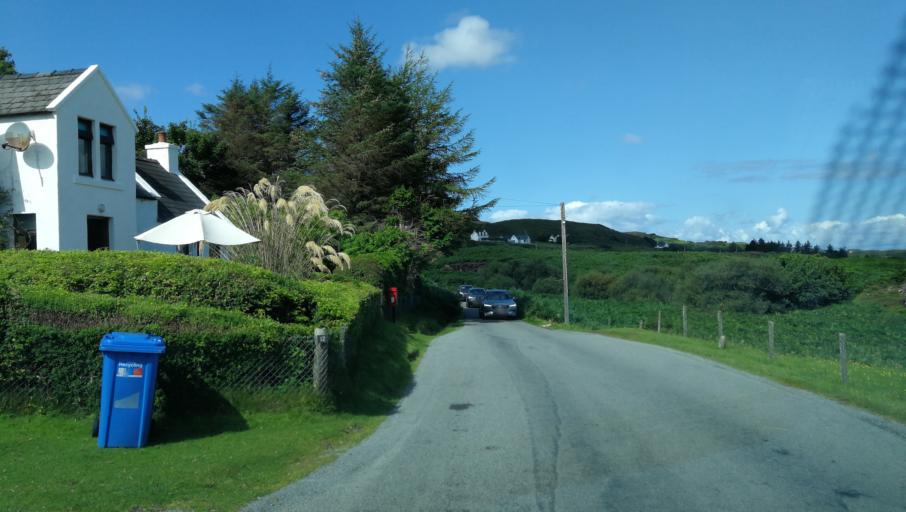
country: GB
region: Scotland
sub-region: Highland
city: Isle of Skye
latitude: 57.4380
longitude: -6.6336
